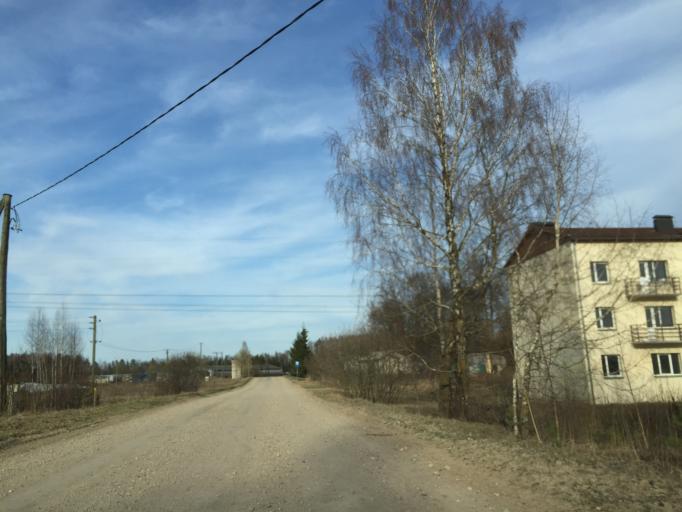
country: LV
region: Kegums
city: Kegums
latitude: 56.7896
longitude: 24.6897
